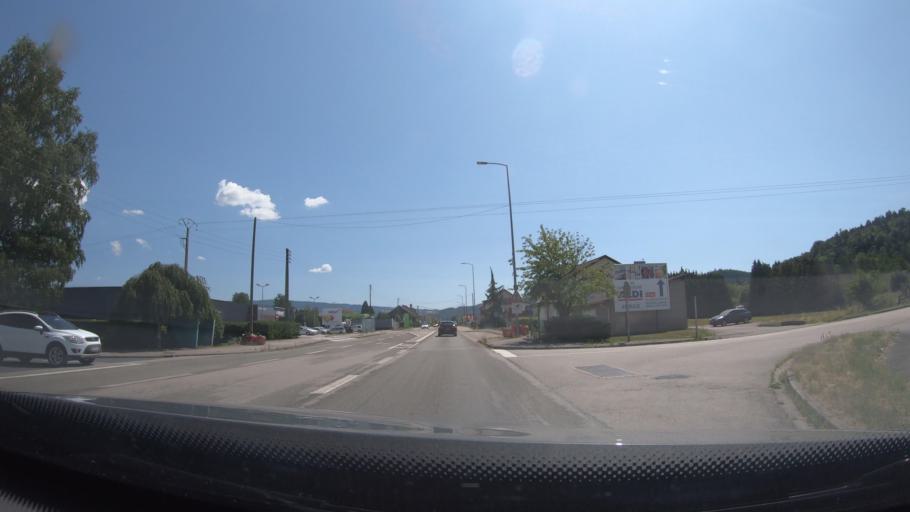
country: FR
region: Lorraine
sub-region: Departement des Vosges
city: Saint-Leonard
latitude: 48.2218
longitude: 6.9452
